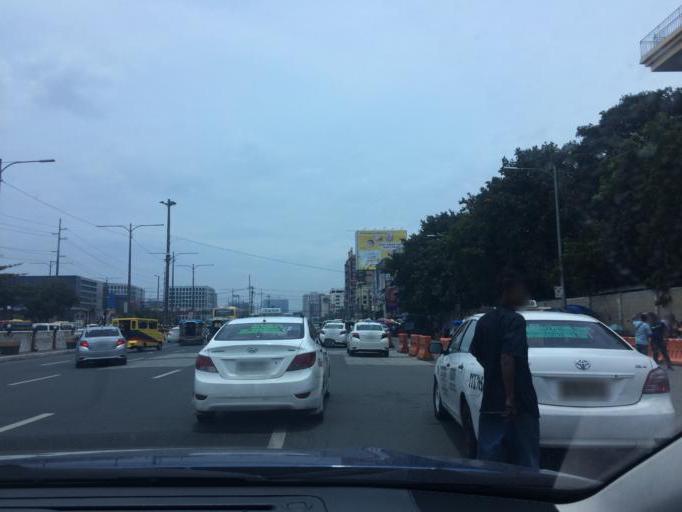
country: PH
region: Metro Manila
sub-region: Makati City
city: Makati City
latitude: 14.5313
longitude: 120.9935
